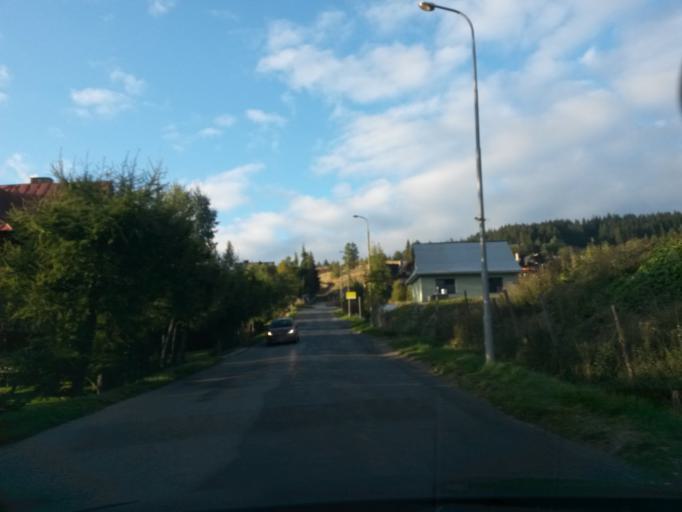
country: PL
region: Lesser Poland Voivodeship
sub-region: Powiat tatrzanski
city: Koscielisko
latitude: 49.2935
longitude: 19.9021
